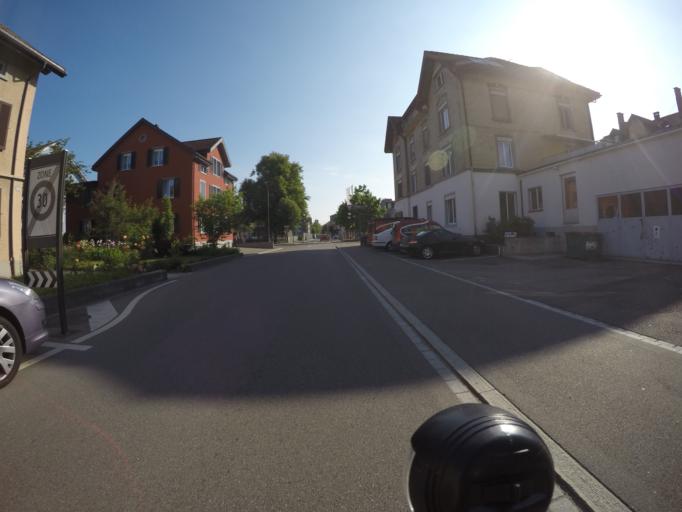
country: CH
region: Zurich
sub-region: Bezirk Winterthur
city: Stadt Winterthur (Kreis 1) / Toessfeld
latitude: 47.4915
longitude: 8.7136
